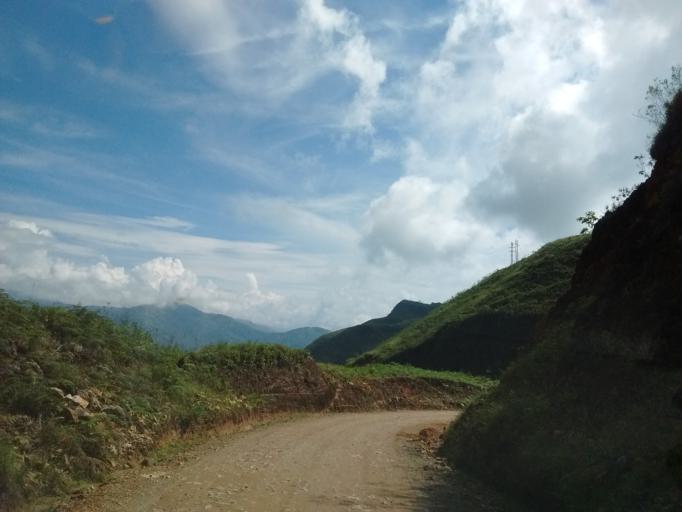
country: CO
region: Cauca
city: Morales
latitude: 2.6882
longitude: -76.7441
